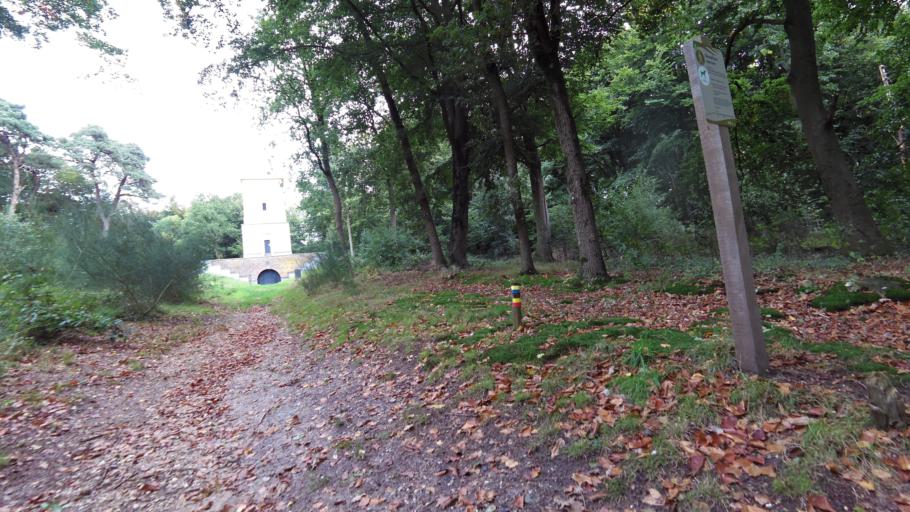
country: NL
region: Utrecht
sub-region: Gemeente Utrechtse Heuvelrug
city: Leersum
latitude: 52.0175
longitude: 5.4209
